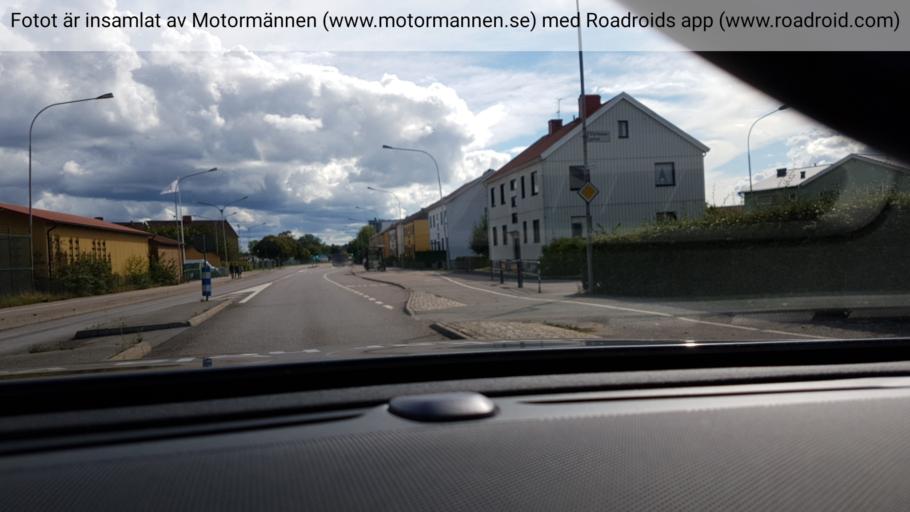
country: SE
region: Vaestra Goetaland
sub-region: Vanersborgs Kommun
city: Vanersborg
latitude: 58.3710
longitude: 12.3234
